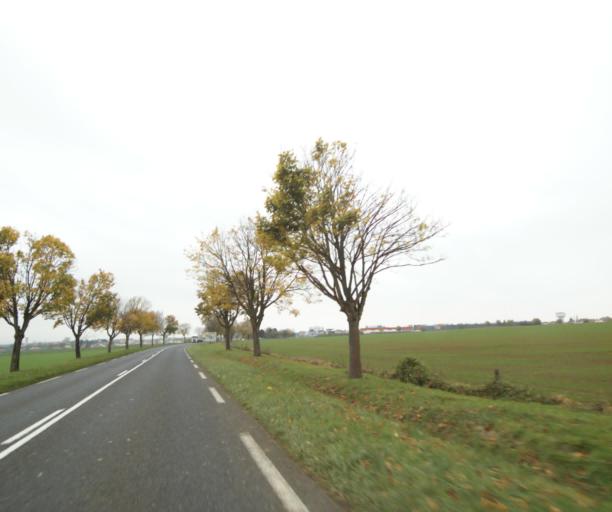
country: FR
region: Lorraine
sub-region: Departement de Meurthe-et-Moselle
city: Briey
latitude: 49.2586
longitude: 5.9500
